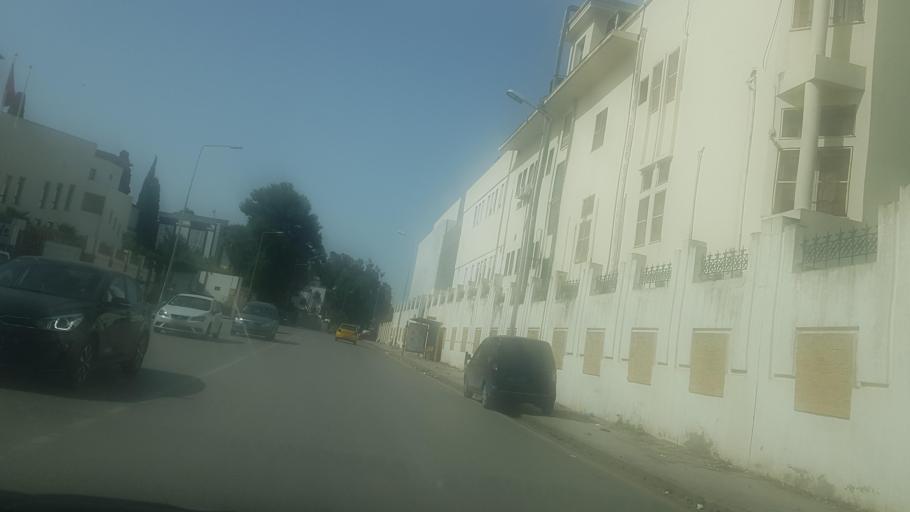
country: TN
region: Tunis
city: Tunis
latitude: 36.8235
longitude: 10.1787
